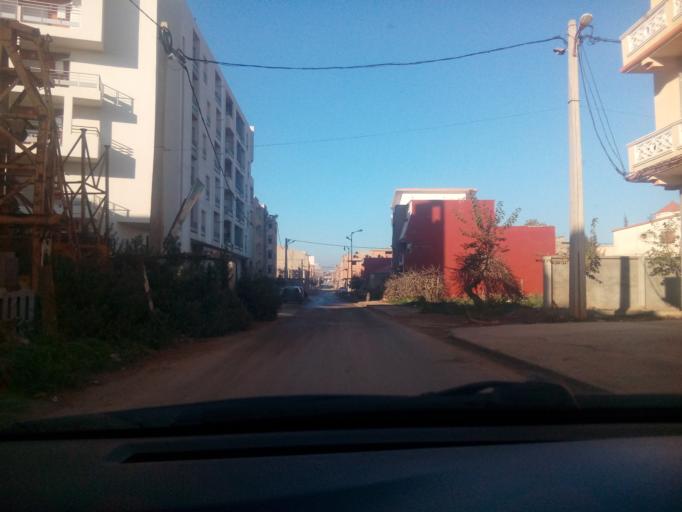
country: DZ
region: Oran
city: Bir el Djir
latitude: 35.7556
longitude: -0.5314
